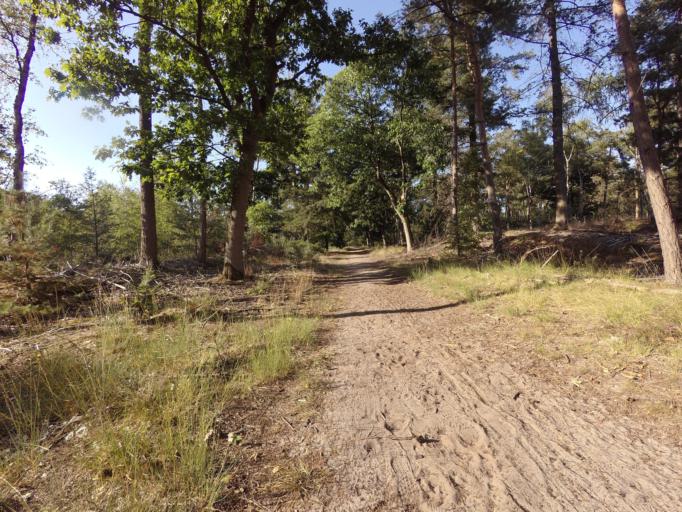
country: NL
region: North Brabant
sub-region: Gemeente Someren
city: Someren
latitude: 51.3766
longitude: 5.6558
